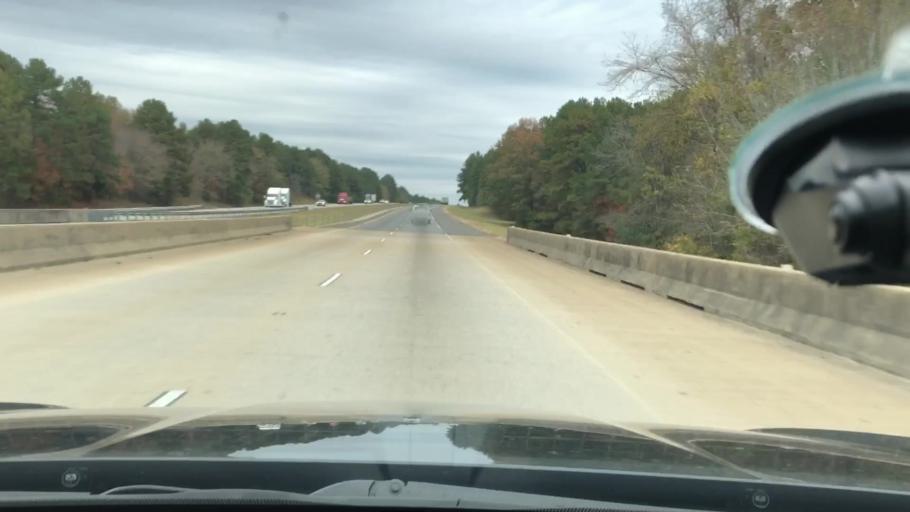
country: US
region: Arkansas
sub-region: Hot Spring County
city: Malvern
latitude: 34.3173
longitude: -92.9343
